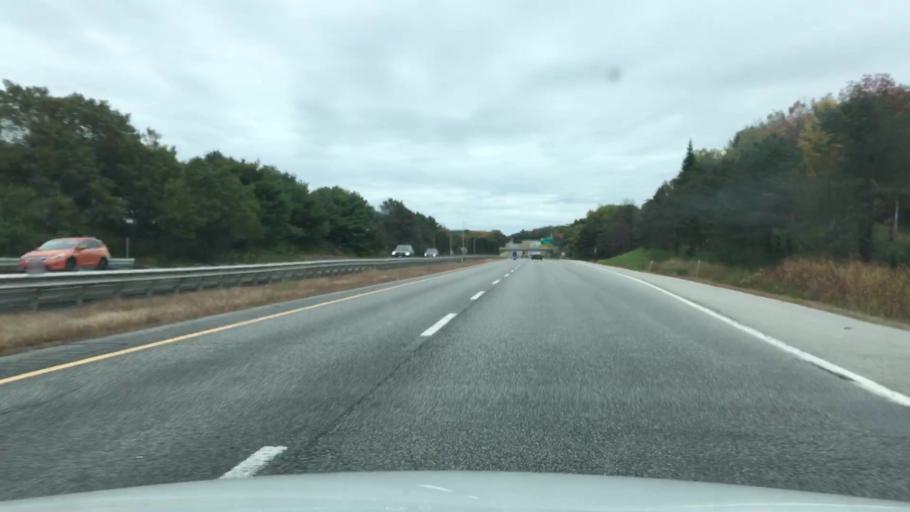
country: US
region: Maine
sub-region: Sagadahoc County
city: Topsham
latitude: 43.9150
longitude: -70.0285
